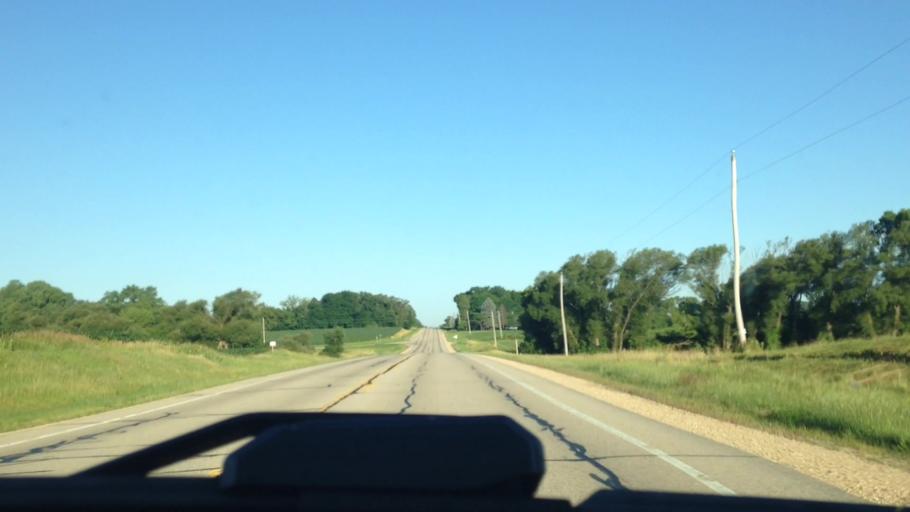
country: US
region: Wisconsin
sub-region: Columbia County
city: Fall River
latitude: 43.3416
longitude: -89.0650
